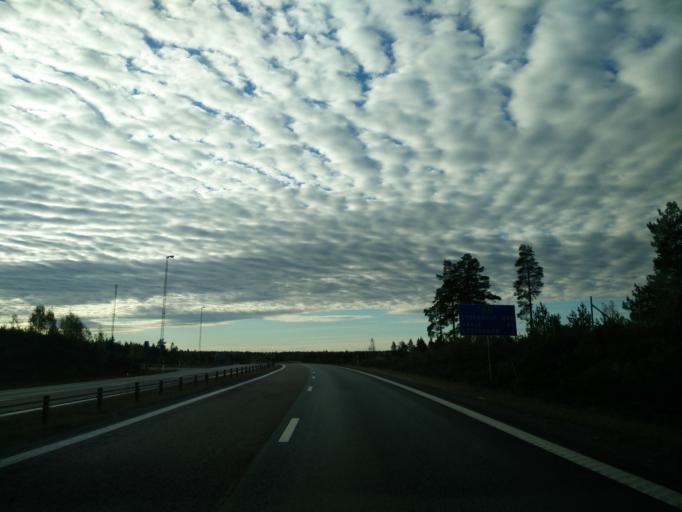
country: SE
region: Gaevleborg
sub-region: Soderhamns Kommun
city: Soderhamn
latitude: 61.3380
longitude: 17.0164
